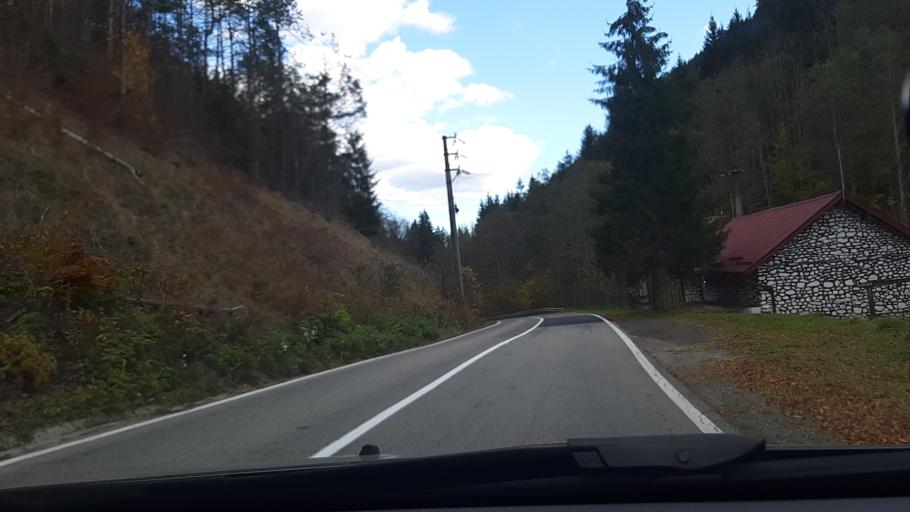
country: RO
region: Valcea
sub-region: Comuna Voineasa
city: Voineasa
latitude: 45.4315
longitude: 23.8973
